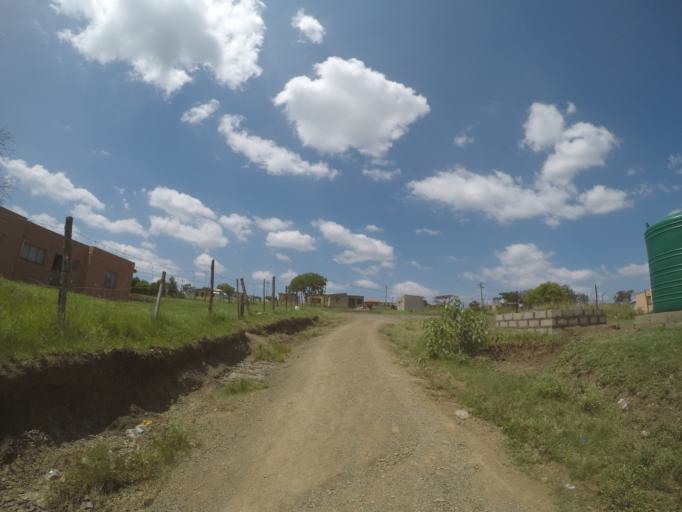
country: ZA
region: KwaZulu-Natal
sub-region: uThungulu District Municipality
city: Empangeni
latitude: -28.6031
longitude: 31.7404
